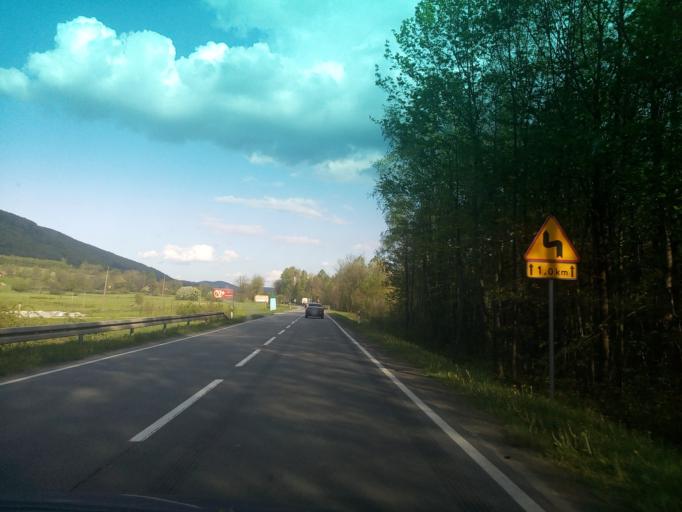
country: PL
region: Lesser Poland Voivodeship
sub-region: Powiat nowosadecki
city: Kamionka Wielka
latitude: 49.5412
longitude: 20.7945
